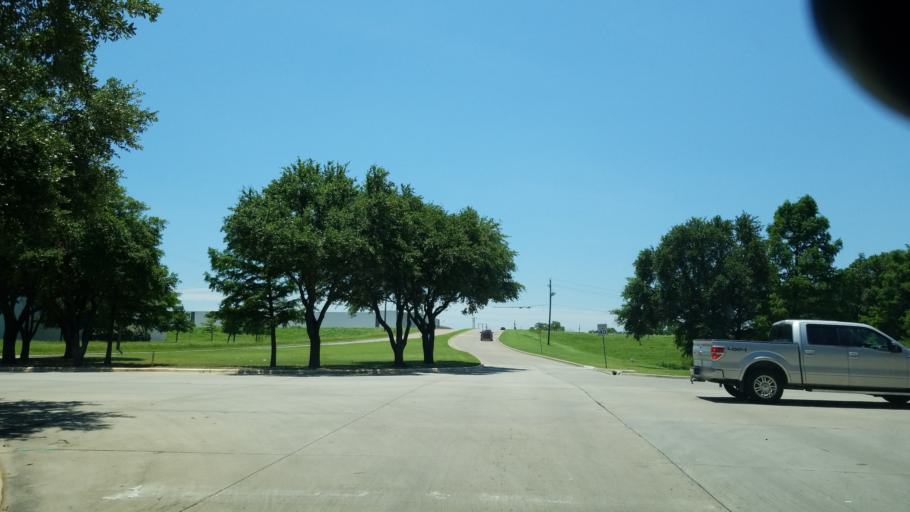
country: US
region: Texas
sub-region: Dallas County
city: Farmers Branch
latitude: 32.9286
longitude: -96.9097
